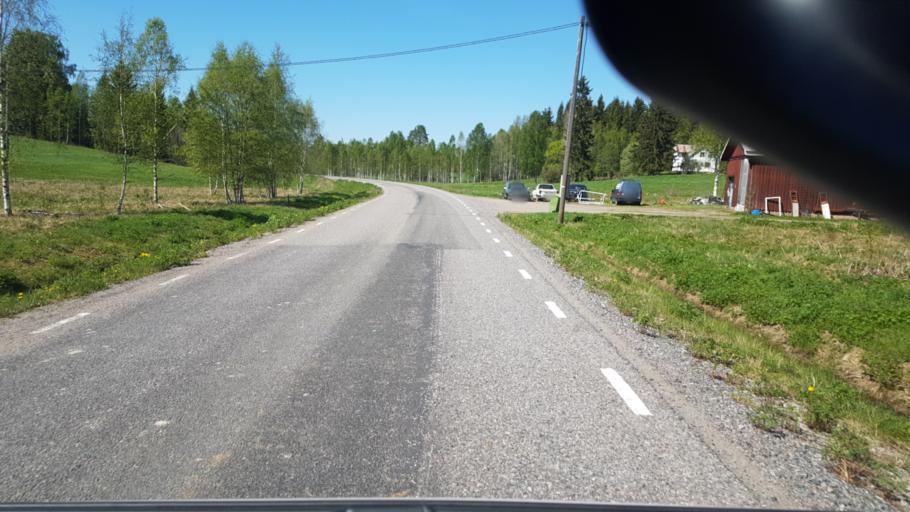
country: SE
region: Vaermland
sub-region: Eda Kommun
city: Charlottenberg
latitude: 59.9935
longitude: 12.3922
